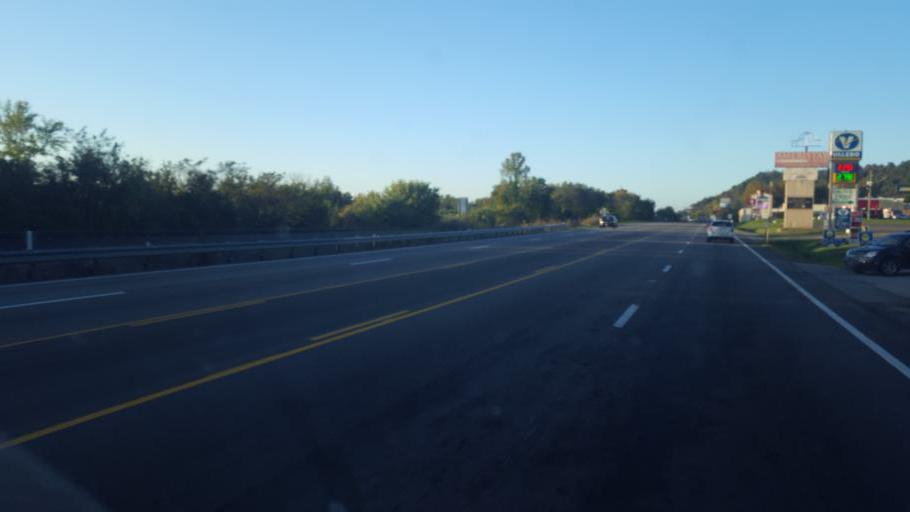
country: US
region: Ohio
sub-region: Scioto County
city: Rosemount
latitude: 38.7816
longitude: -82.9850
